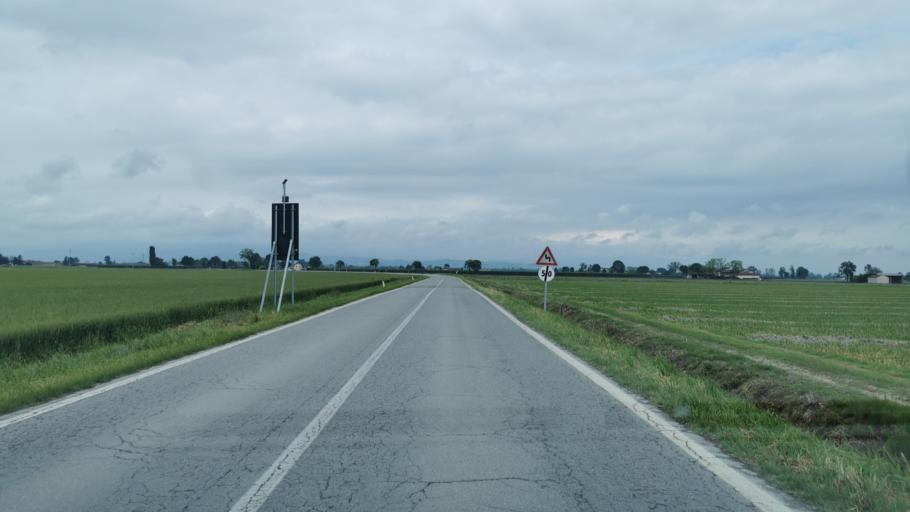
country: IT
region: Piedmont
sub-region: Provincia di Cuneo
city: Genola
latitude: 44.6103
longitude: 7.6147
